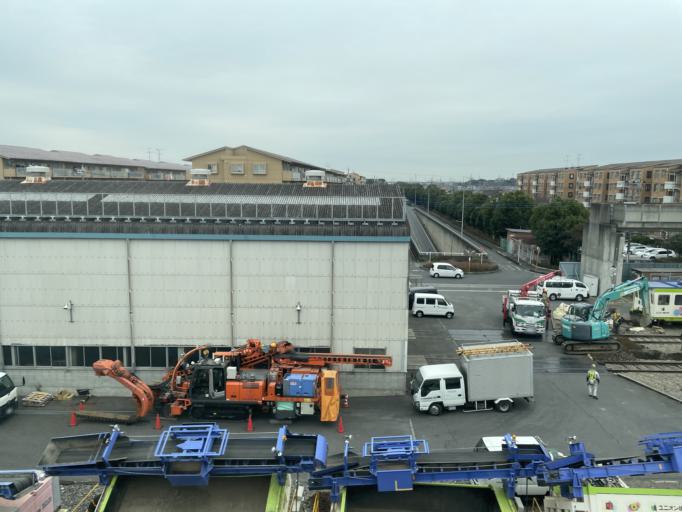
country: JP
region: Saitama
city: Kukichuo
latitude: 36.0880
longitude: 139.6797
